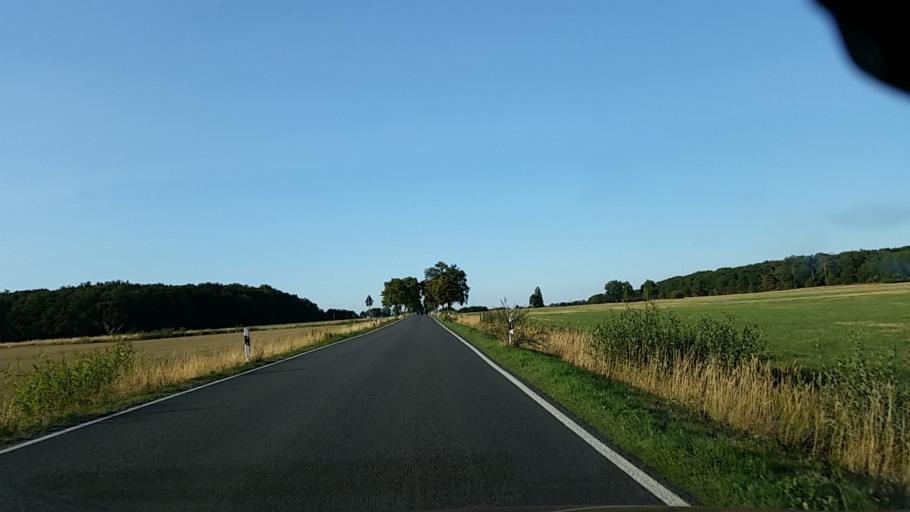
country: DE
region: Lower Saxony
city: Lehre
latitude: 52.3497
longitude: 10.6255
